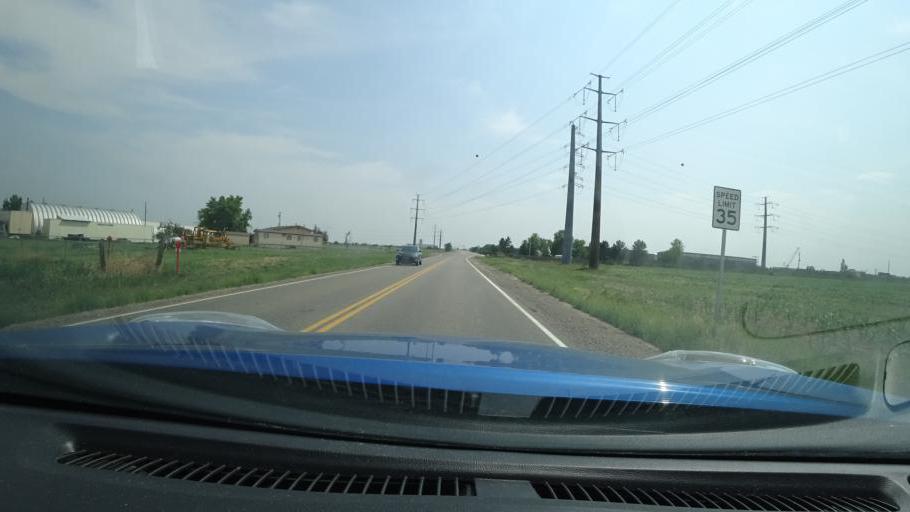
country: US
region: Colorado
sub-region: Adams County
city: Aurora
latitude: 39.7559
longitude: -104.7347
